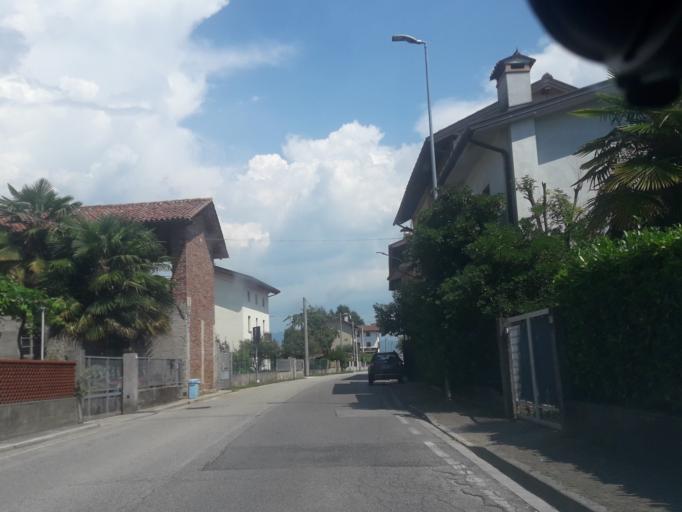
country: IT
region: Friuli Venezia Giulia
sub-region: Provincia di Udine
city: Reana del Roiale
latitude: 46.1281
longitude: 13.2151
